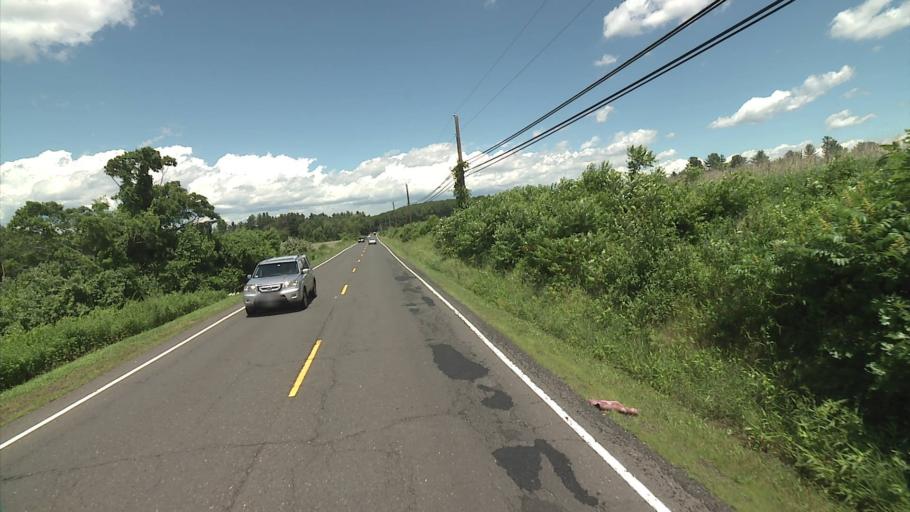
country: US
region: Massachusetts
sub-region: Hampden County
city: East Longmeadow
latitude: 42.0244
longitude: -72.5151
